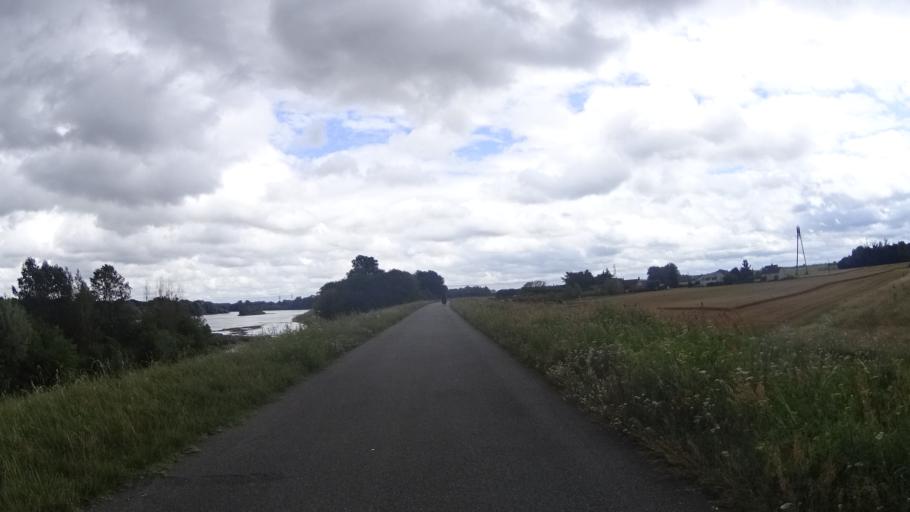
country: FR
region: Centre
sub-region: Departement du Loiret
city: Mareau-aux-Pres
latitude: 47.8634
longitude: 1.7869
